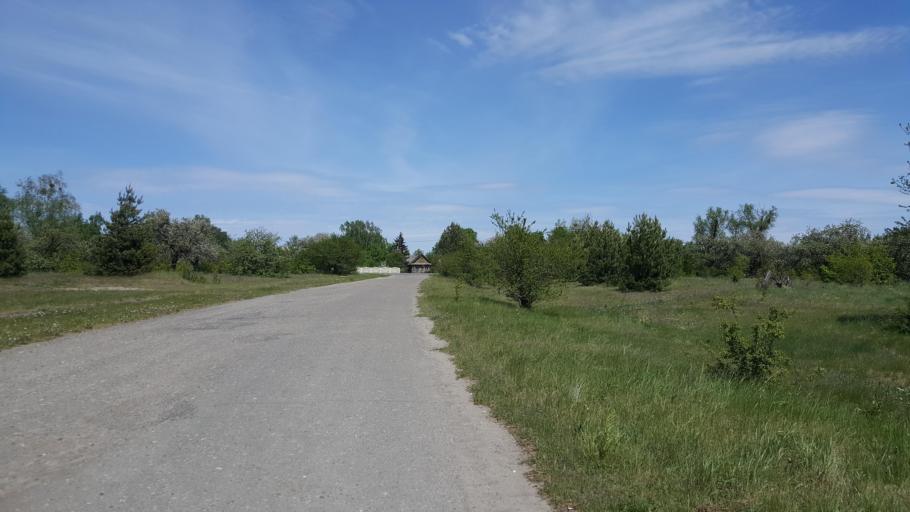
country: BY
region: Brest
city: Kobryn
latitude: 52.3516
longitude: 24.1875
